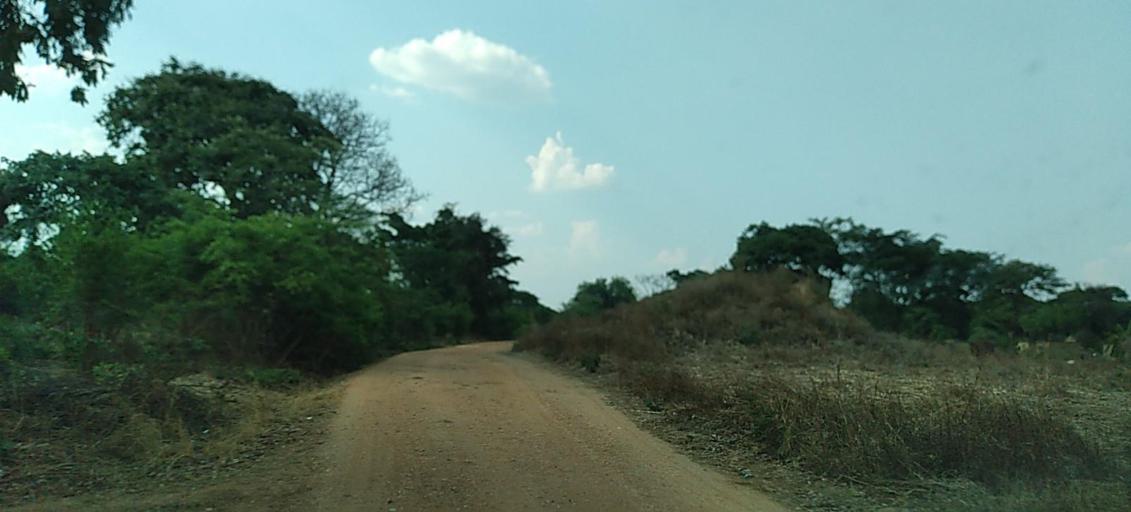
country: ZM
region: Copperbelt
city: Mpongwe
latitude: -13.4883
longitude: 28.0843
